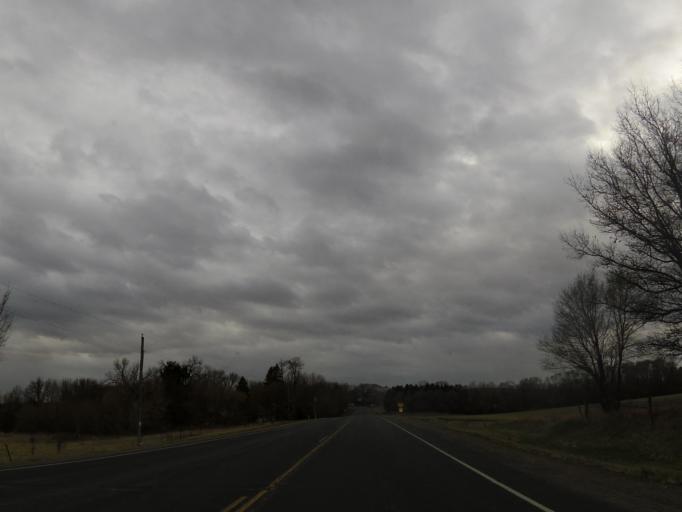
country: US
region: Wisconsin
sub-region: Saint Croix County
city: New Richmond
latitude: 45.0706
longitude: -92.5938
